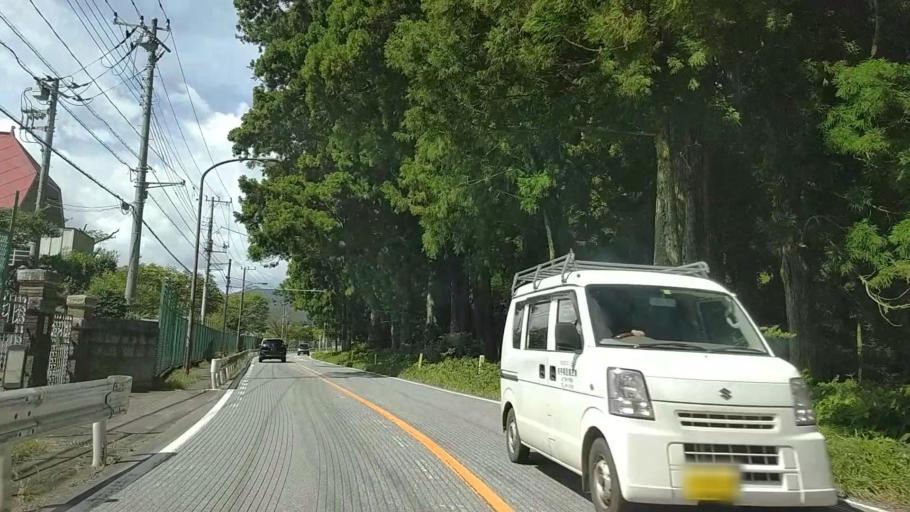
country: JP
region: Tochigi
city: Imaichi
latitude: 36.7275
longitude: 139.6803
